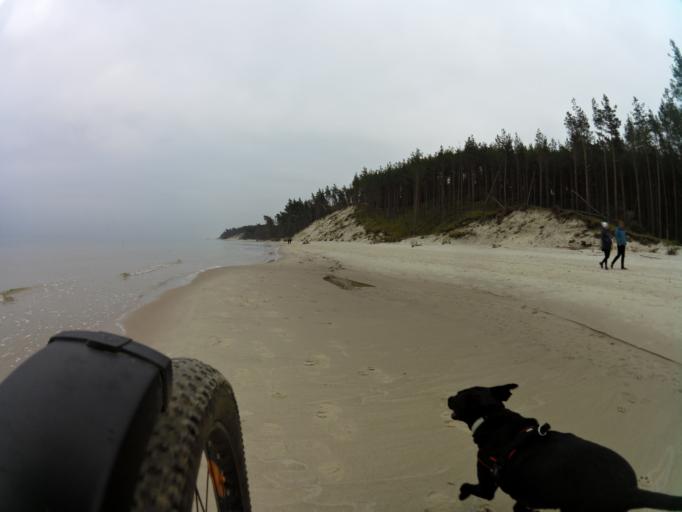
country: PL
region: Pomeranian Voivodeship
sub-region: Powiat pucki
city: Krokowa
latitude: 54.8317
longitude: 18.1332
